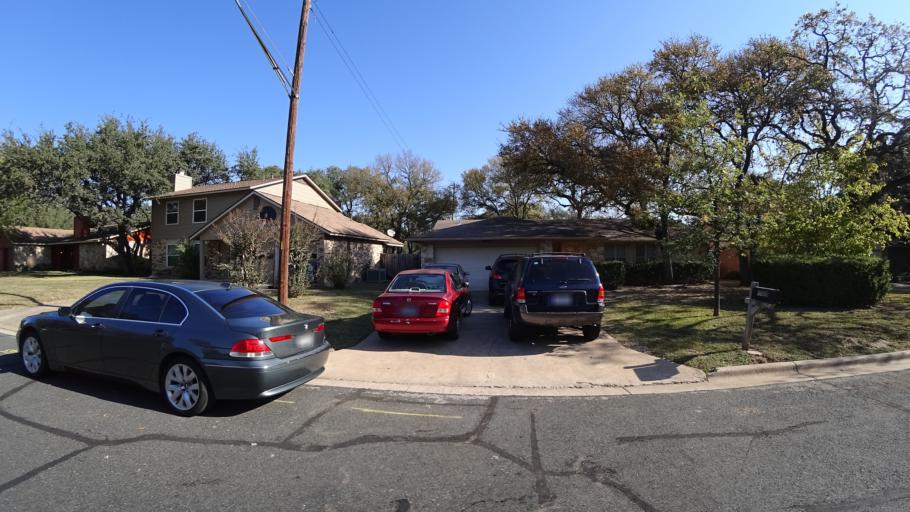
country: US
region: Texas
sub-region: Travis County
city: Barton Creek
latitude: 30.2272
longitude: -97.8434
